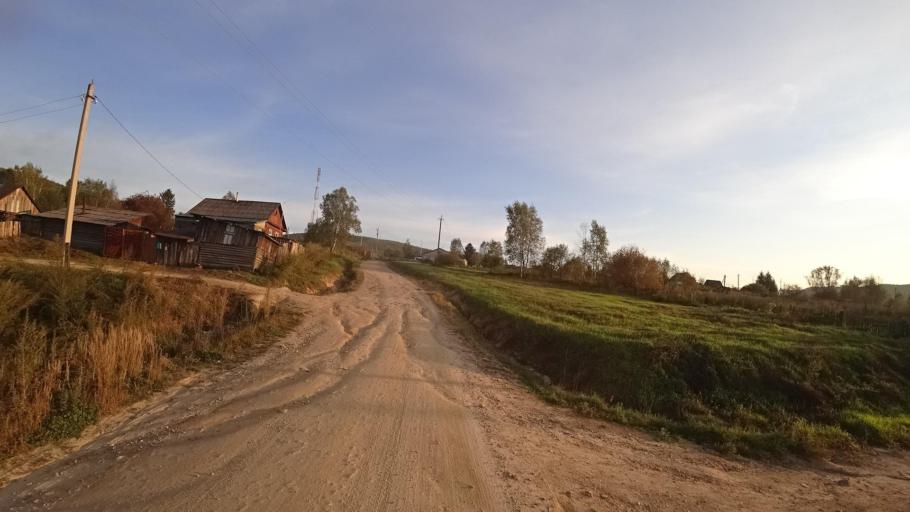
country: RU
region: Jewish Autonomous Oblast
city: Kul'dur
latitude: 49.2055
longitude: 131.6399
